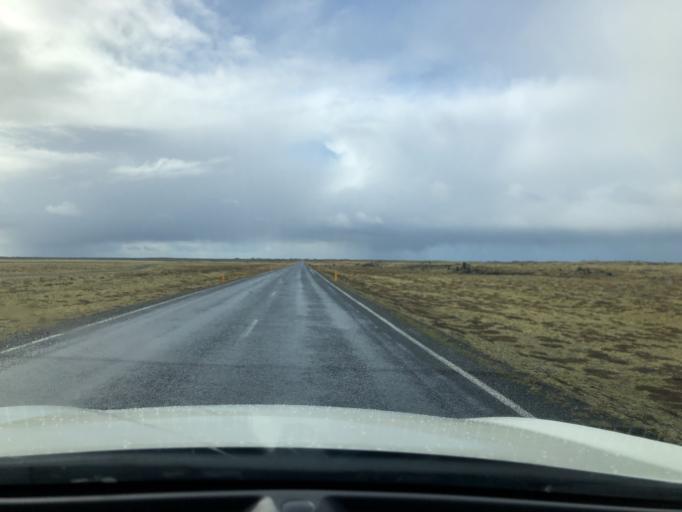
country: IS
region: South
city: Vestmannaeyjar
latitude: 63.5775
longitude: -18.4497
